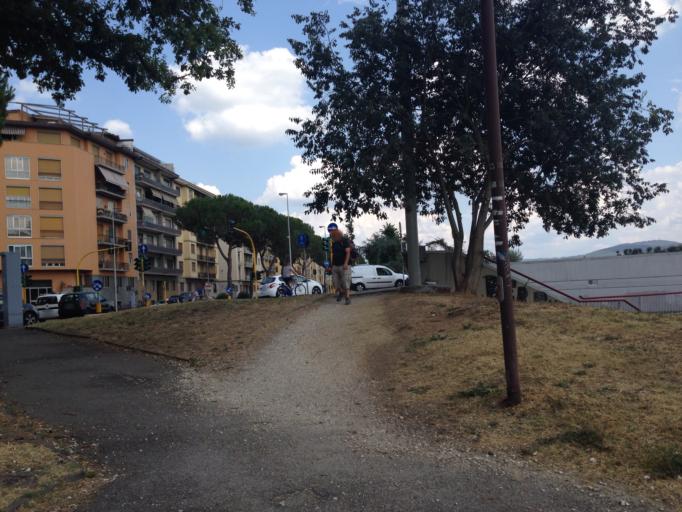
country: IT
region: Tuscany
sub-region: Province of Florence
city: Grassina Ponte a Ema
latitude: 43.7655
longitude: 11.2813
